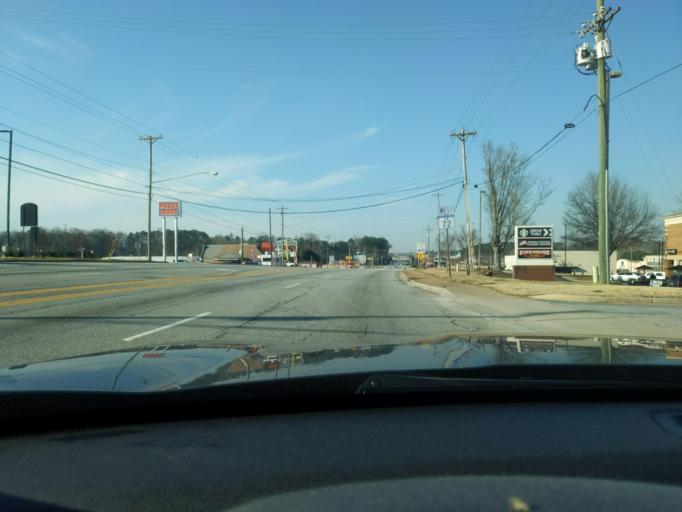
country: US
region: South Carolina
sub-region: Greenwood County
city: Greenwood
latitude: 34.2113
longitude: -82.1782
